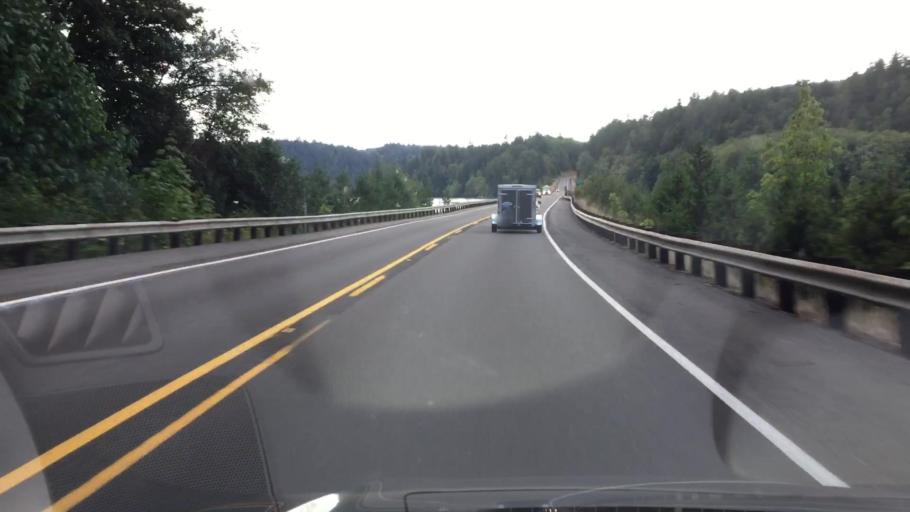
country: US
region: Washington
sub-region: Lewis County
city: Morton
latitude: 46.5170
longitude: -122.5620
